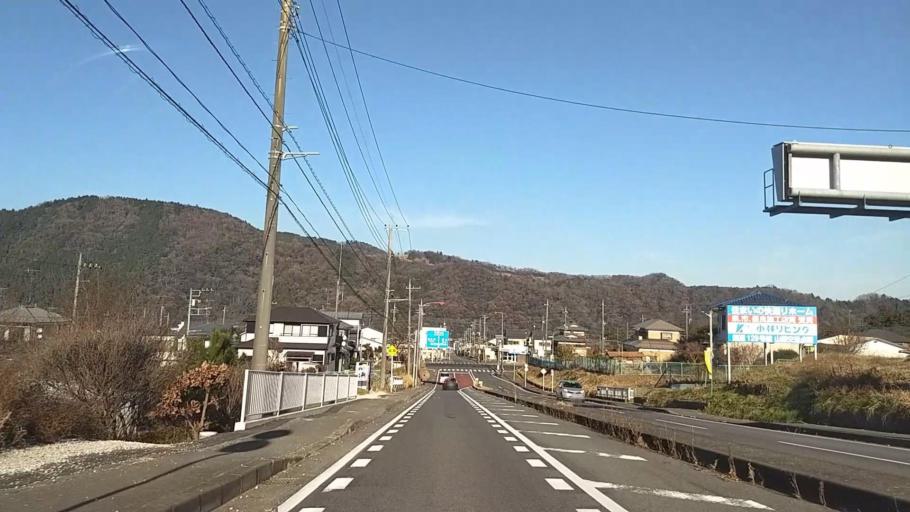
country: JP
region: Kanagawa
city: Zama
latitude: 35.5347
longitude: 139.2707
